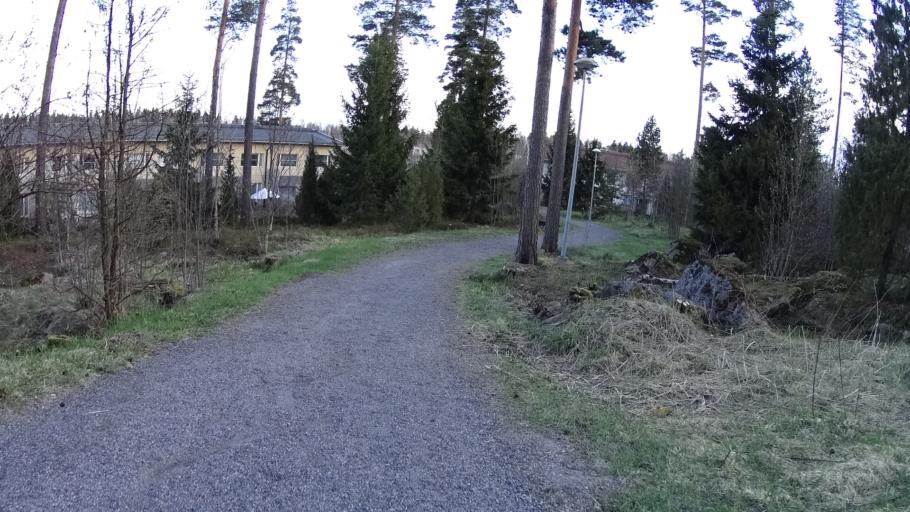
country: FI
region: Uusimaa
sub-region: Helsinki
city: Kilo
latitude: 60.2339
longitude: 24.7802
